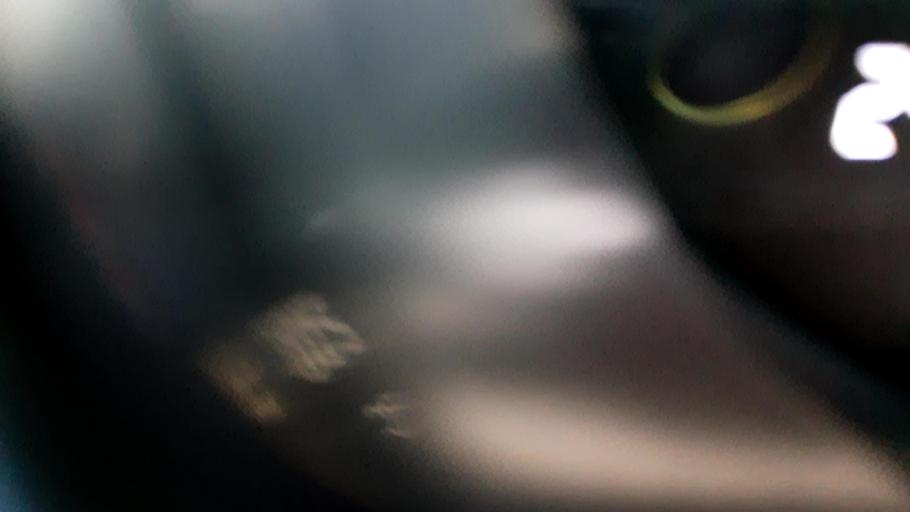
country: RU
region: Nizjnij Novgorod
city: Bor
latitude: 56.3583
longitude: 44.0733
